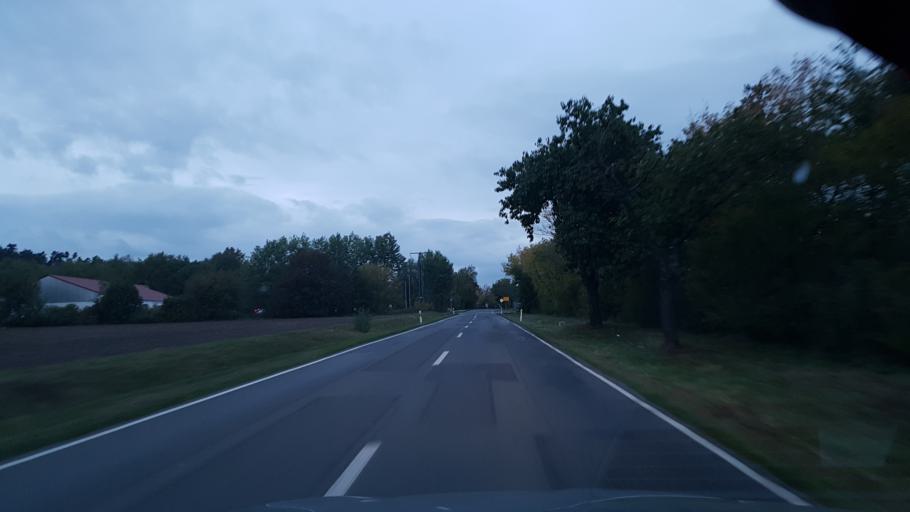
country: DE
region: Brandenburg
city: Groden
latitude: 51.4002
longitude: 13.5852
